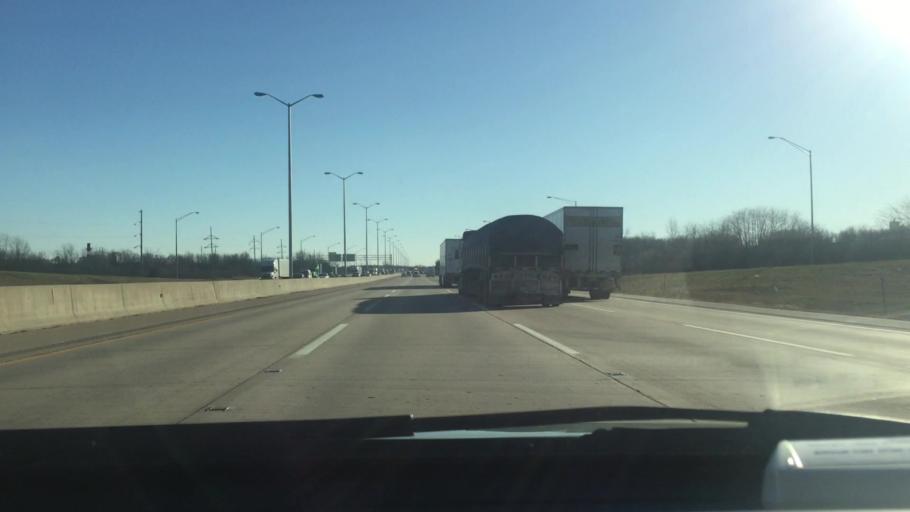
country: US
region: Illinois
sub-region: Lake County
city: Green Oaks
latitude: 42.3108
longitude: -87.9048
